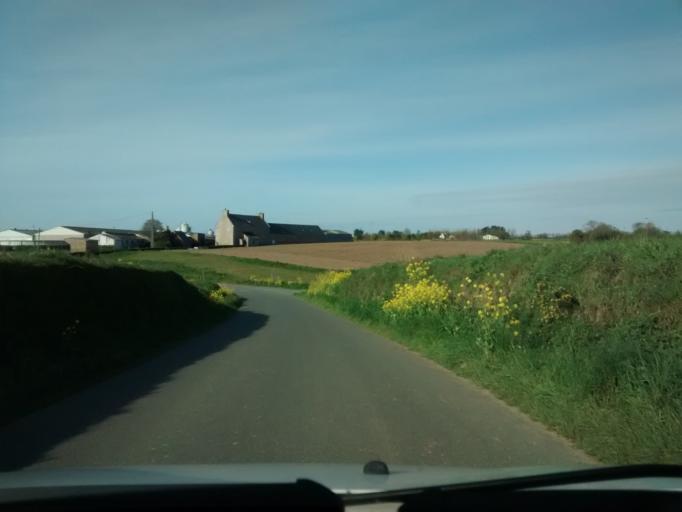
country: FR
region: Brittany
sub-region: Departement des Cotes-d'Armor
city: Penvenan
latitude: 48.7902
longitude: -3.3050
